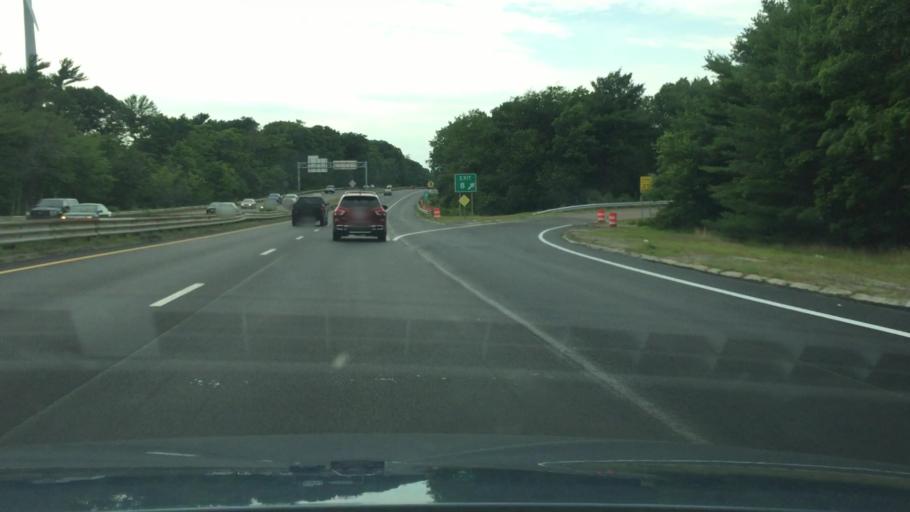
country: US
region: Massachusetts
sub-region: Plymouth County
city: Kingston
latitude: 41.9769
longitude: -70.7115
